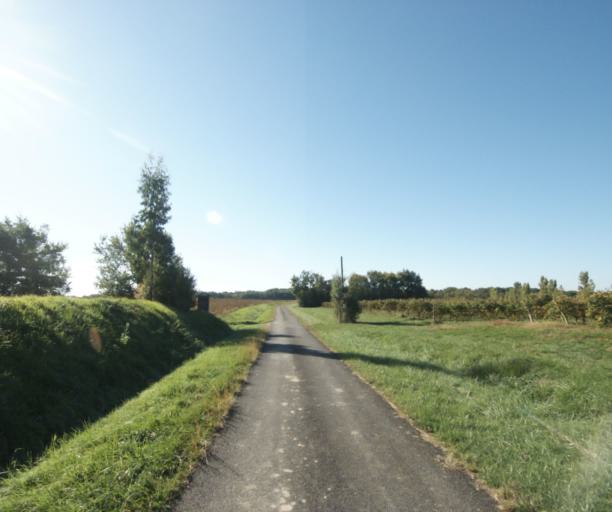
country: FR
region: Midi-Pyrenees
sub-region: Departement du Gers
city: Gondrin
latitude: 43.8183
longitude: 0.2338
